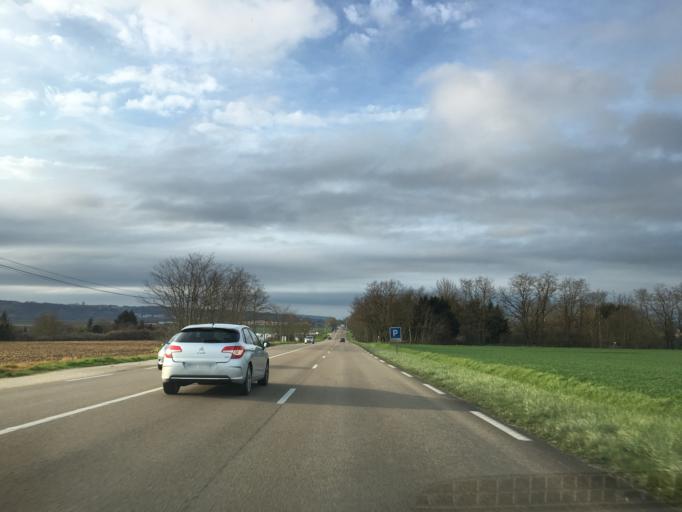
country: FR
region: Bourgogne
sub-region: Departement de l'Yonne
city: Maillot
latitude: 48.1590
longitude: 3.3039
